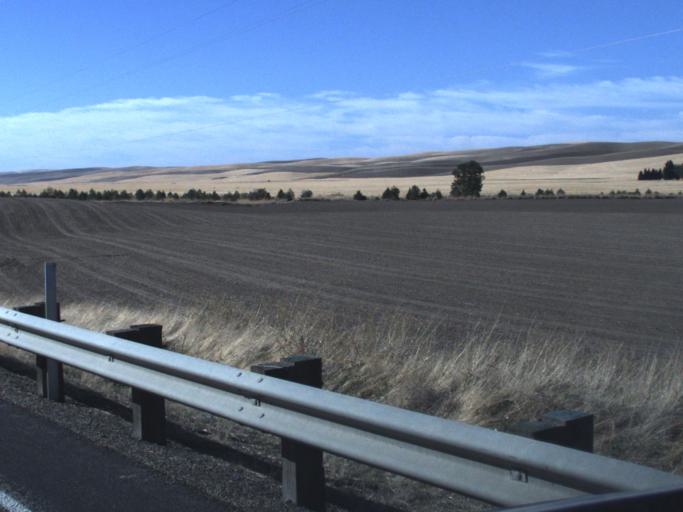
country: US
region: Washington
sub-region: Walla Walla County
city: Waitsburg
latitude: 46.2990
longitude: -118.3214
